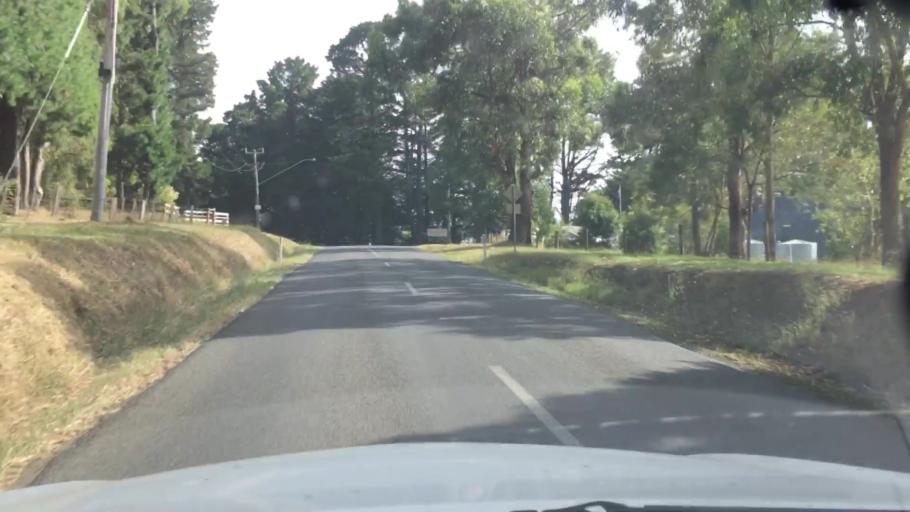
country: AU
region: Victoria
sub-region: Yarra Ranges
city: Macclesfield
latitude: -37.8860
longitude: 145.4767
